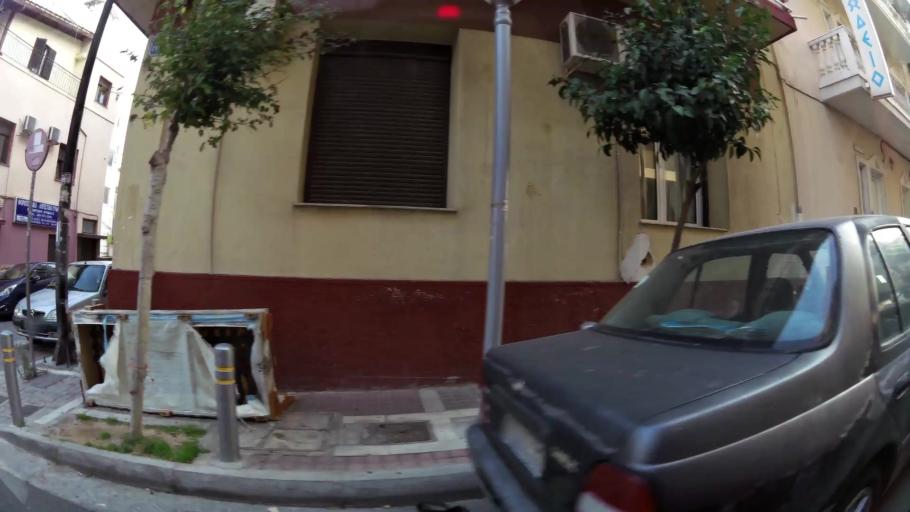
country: GR
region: Attica
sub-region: Nomarchia Athinas
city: Dhafni
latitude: 37.9527
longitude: 23.7366
